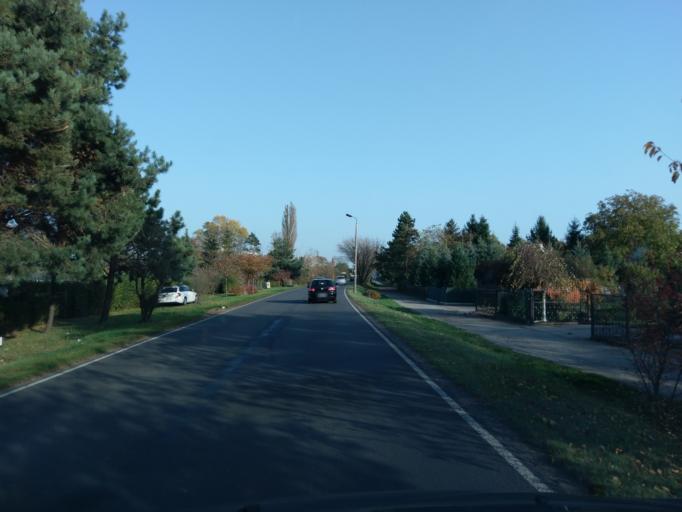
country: DE
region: Brandenburg
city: Herzberg
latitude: 51.6952
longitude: 13.2404
